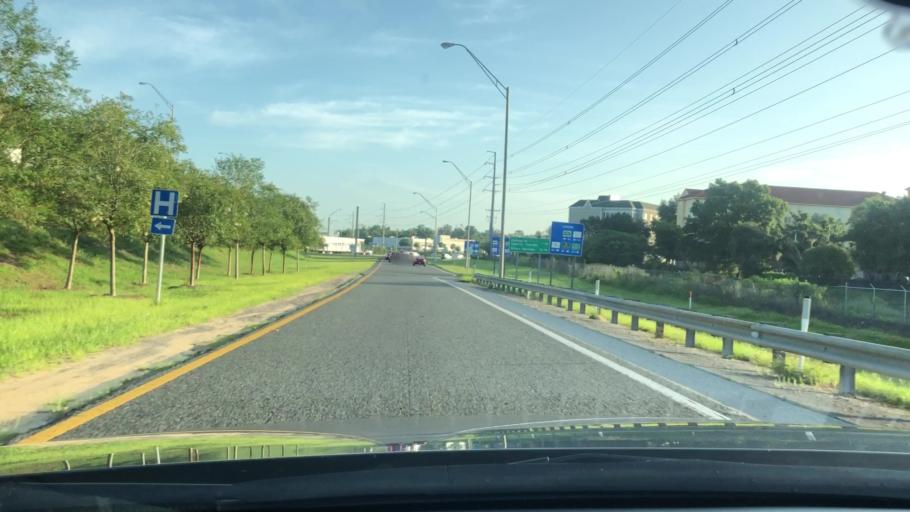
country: US
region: Florida
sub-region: Marion County
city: Ocala
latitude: 29.1485
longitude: -82.1846
